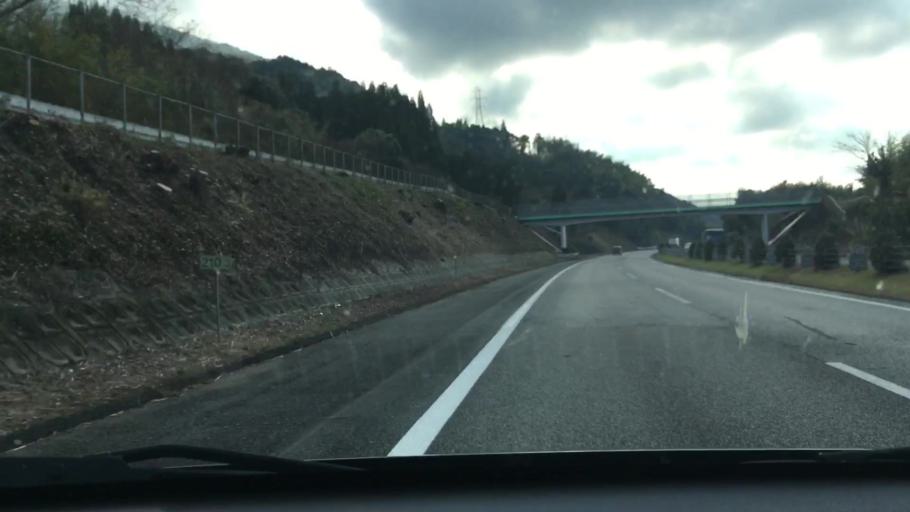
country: JP
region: Kumamoto
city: Yatsushiro
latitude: 32.5338
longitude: 130.6713
